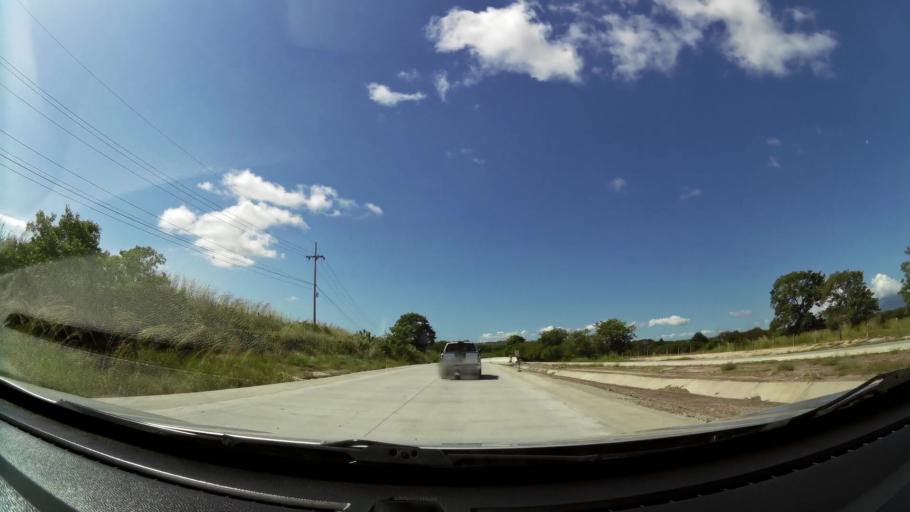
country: CR
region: Guanacaste
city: Bagaces
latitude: 10.5390
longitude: -85.3028
